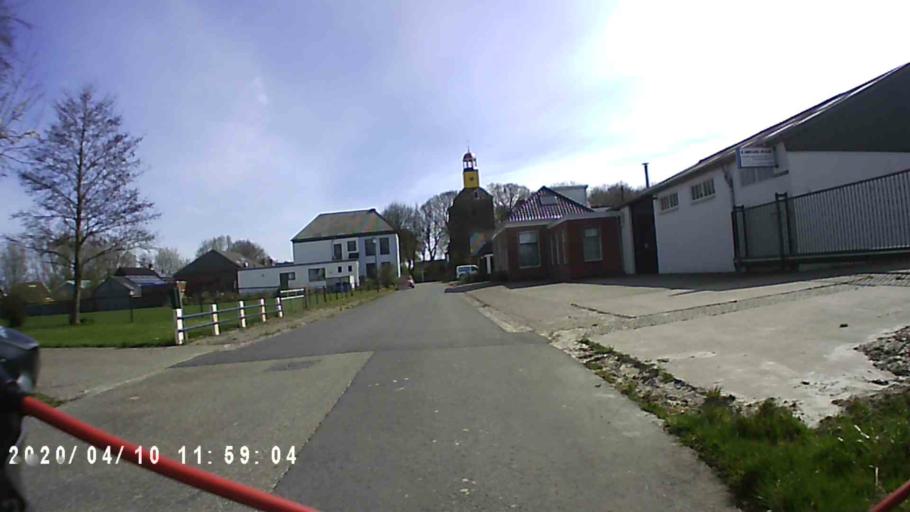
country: NL
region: Groningen
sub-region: Gemeente De Marne
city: Ulrum
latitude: 53.3880
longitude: 6.3576
